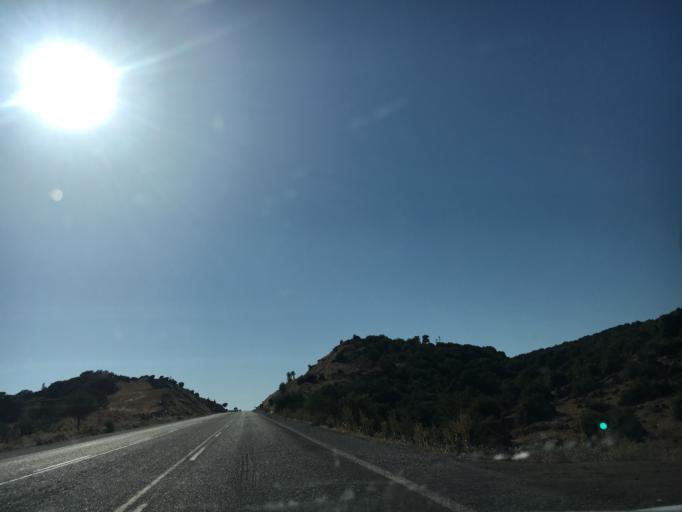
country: TR
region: Canakkale
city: Behram
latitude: 39.5066
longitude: 26.3932
